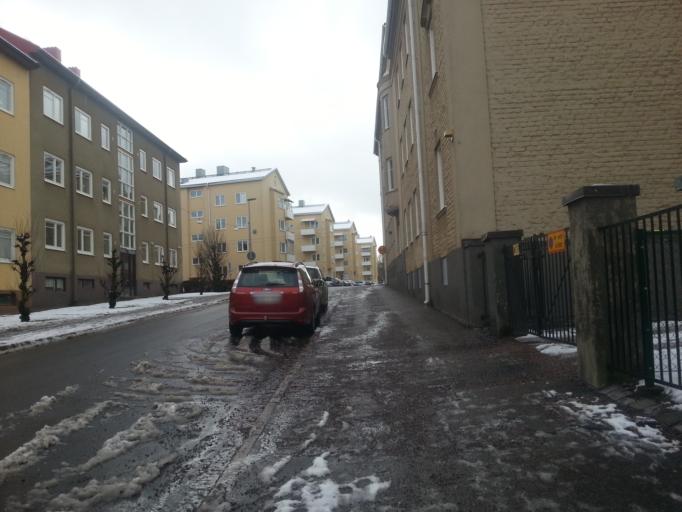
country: SE
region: OEstergoetland
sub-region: Norrkopings Kommun
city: Norrkoping
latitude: 58.5823
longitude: 16.1890
